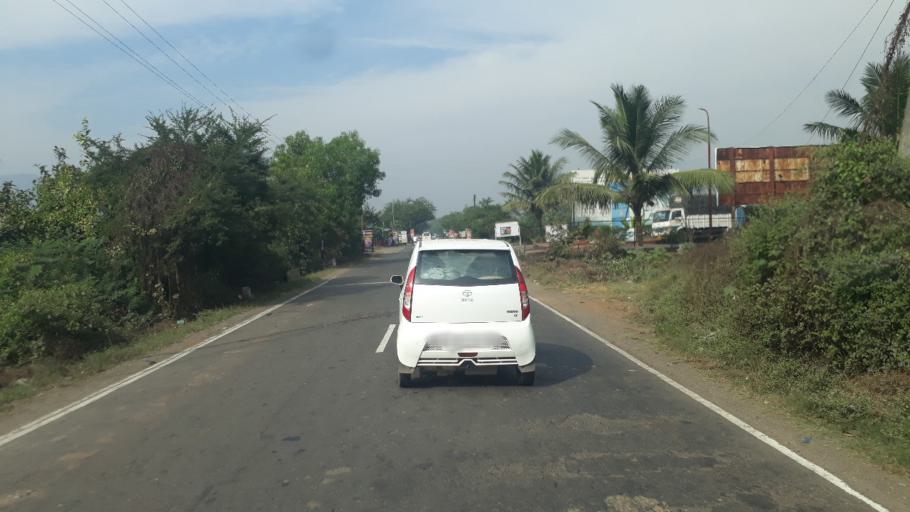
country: IN
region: Maharashtra
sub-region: Raigarh
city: Alibag
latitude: 18.6880
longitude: 72.9809
